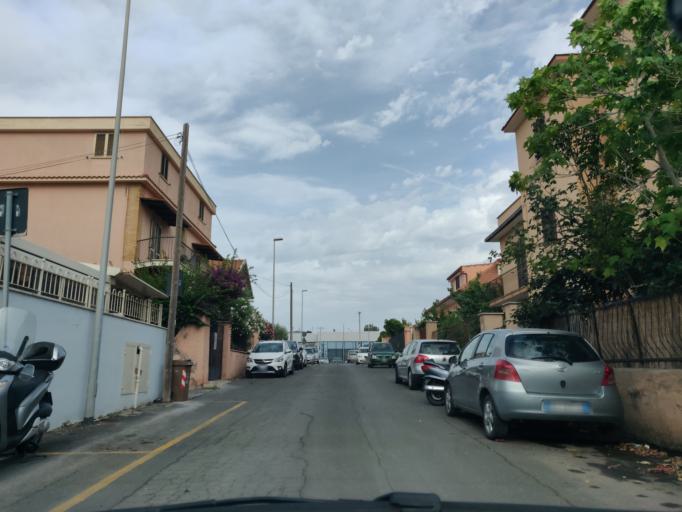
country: IT
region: Latium
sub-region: Citta metropolitana di Roma Capitale
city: Civitavecchia
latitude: 42.0741
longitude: 11.8082
